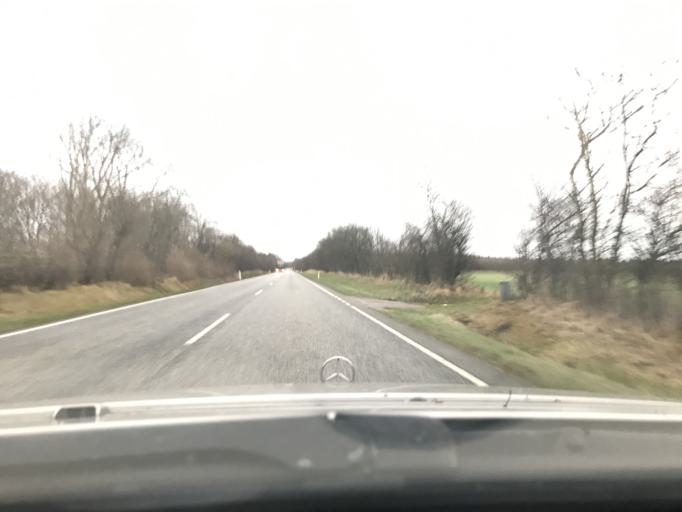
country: DK
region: South Denmark
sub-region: Tonder Kommune
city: Logumkloster
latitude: 55.1799
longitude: 8.9072
